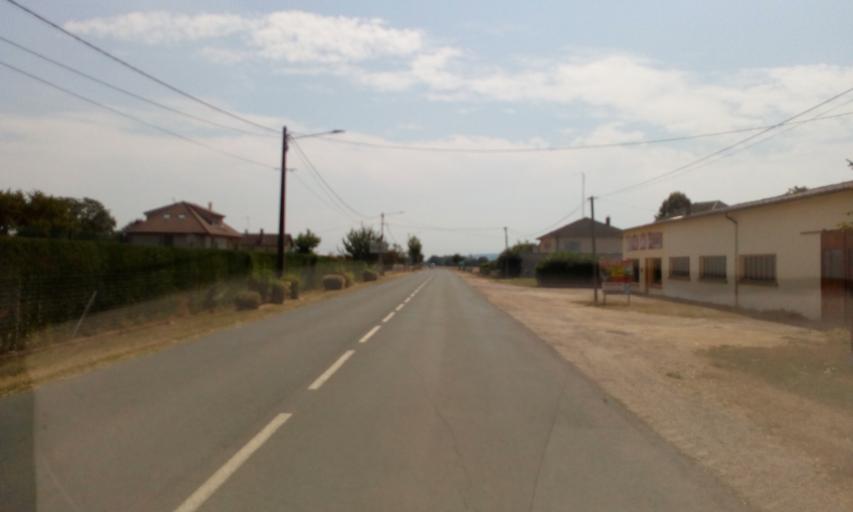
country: FR
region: Lorraine
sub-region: Departement de la Meuse
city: Etain
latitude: 49.0927
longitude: 5.6266
